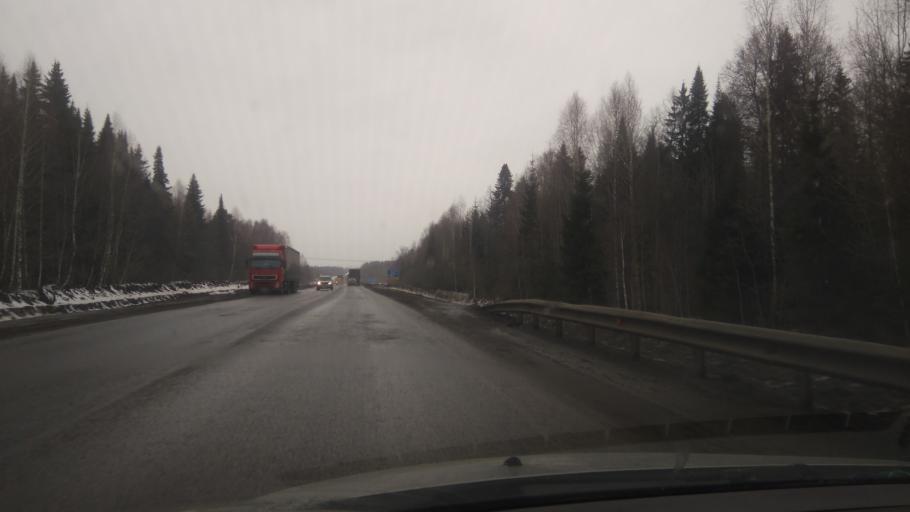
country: RU
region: Perm
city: Kungur
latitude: 57.3228
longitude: 56.9629
